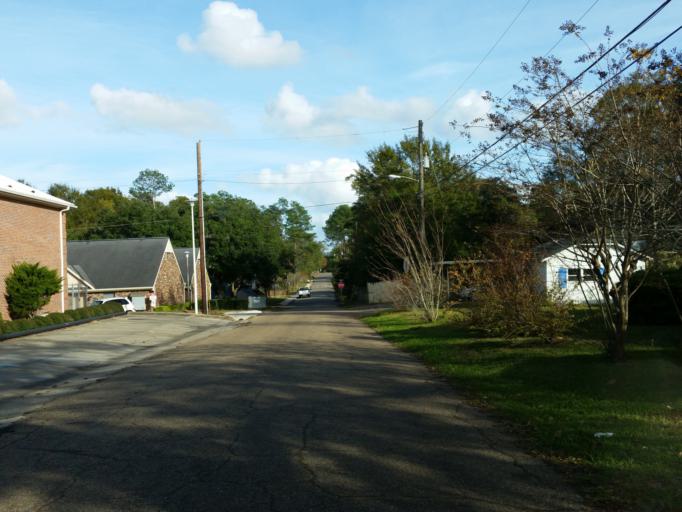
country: US
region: Mississippi
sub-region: Forrest County
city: Hattiesburg
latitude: 31.3229
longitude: -89.3262
